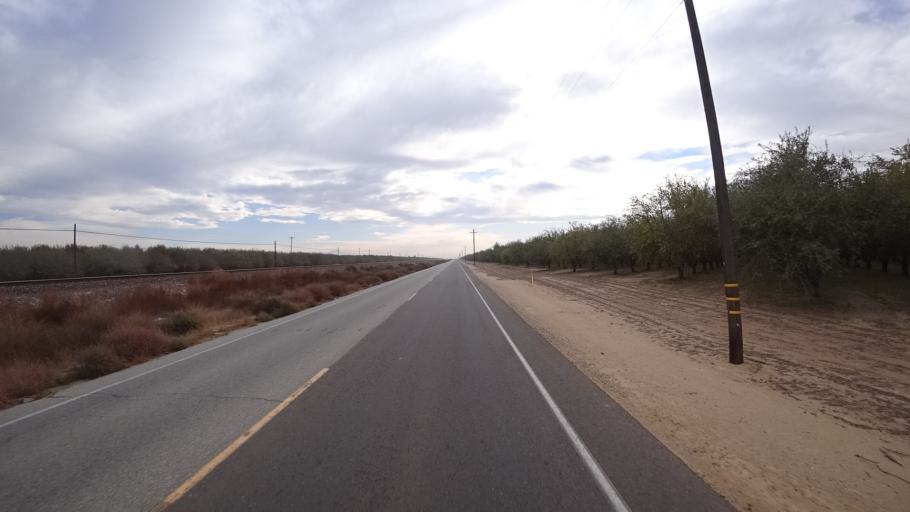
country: US
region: California
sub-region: Kern County
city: Rosedale
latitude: 35.4309
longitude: -119.1862
